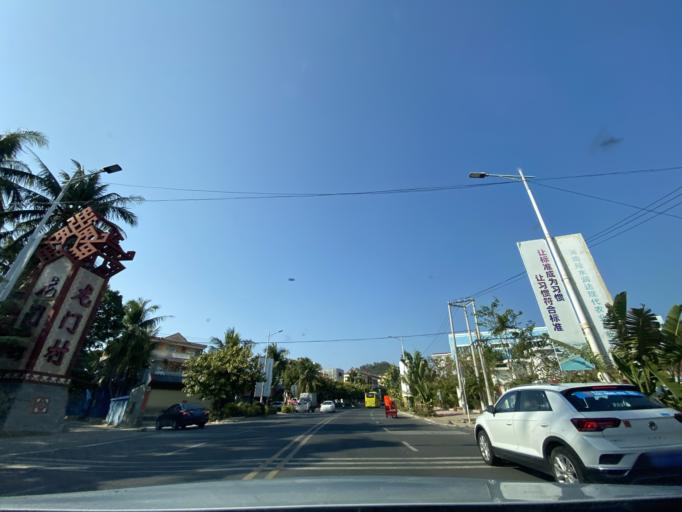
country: CN
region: Hainan
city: Yingzhou
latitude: 18.4382
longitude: 109.8494
